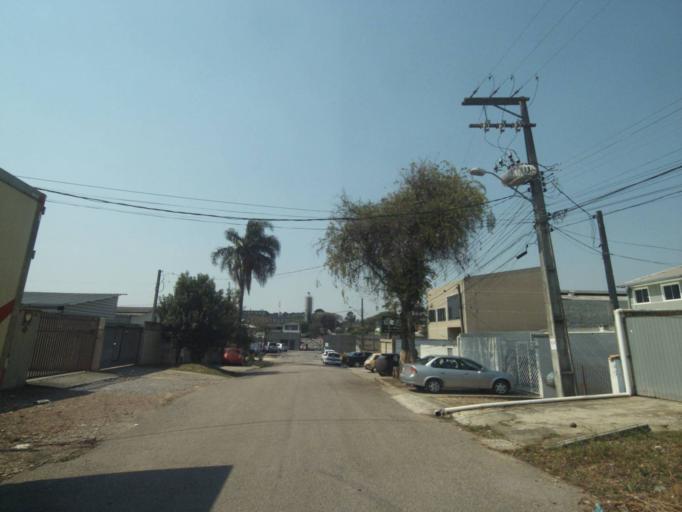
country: BR
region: Parana
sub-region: Sao Jose Dos Pinhais
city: Sao Jose dos Pinhais
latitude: -25.5048
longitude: -49.2812
